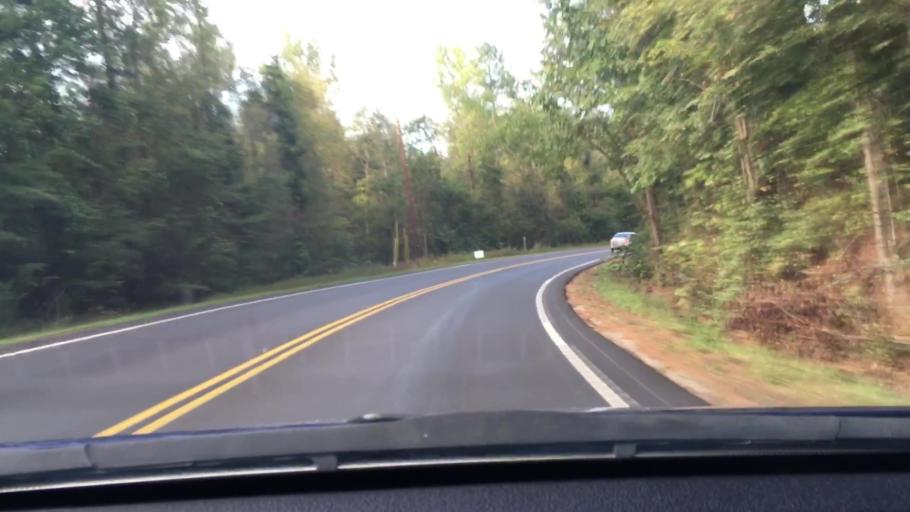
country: US
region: South Carolina
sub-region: Lexington County
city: Irmo
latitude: 34.1082
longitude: -81.1619
